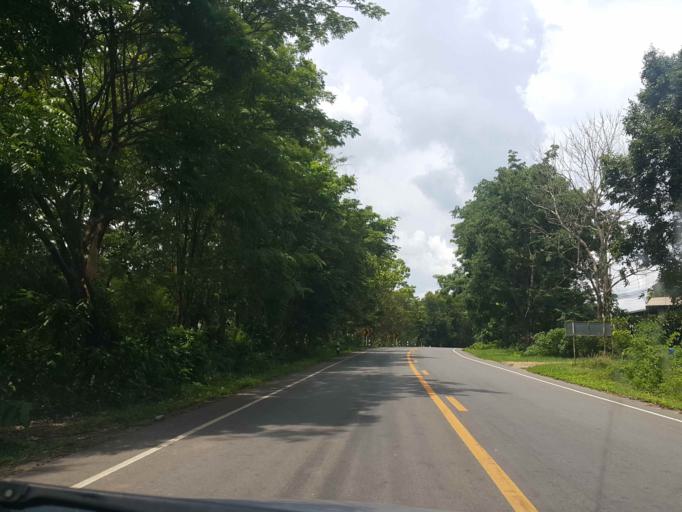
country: TH
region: Nan
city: Ban Luang
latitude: 18.8530
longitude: 100.4472
